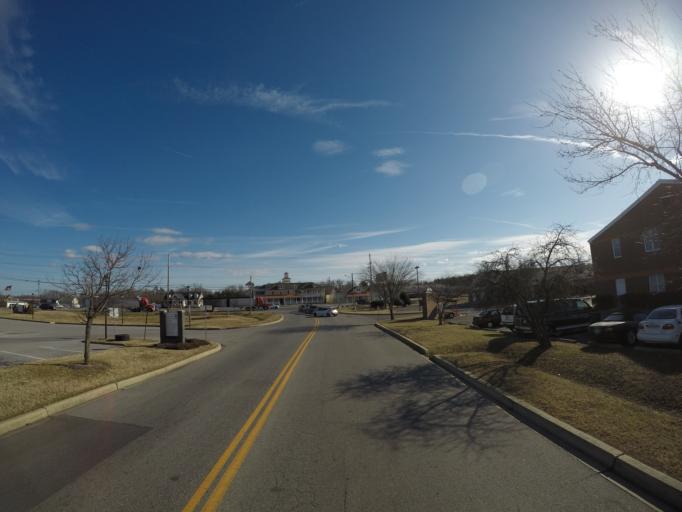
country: US
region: Maryland
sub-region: Charles County
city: Saint Charles
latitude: 38.5884
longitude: -76.9457
